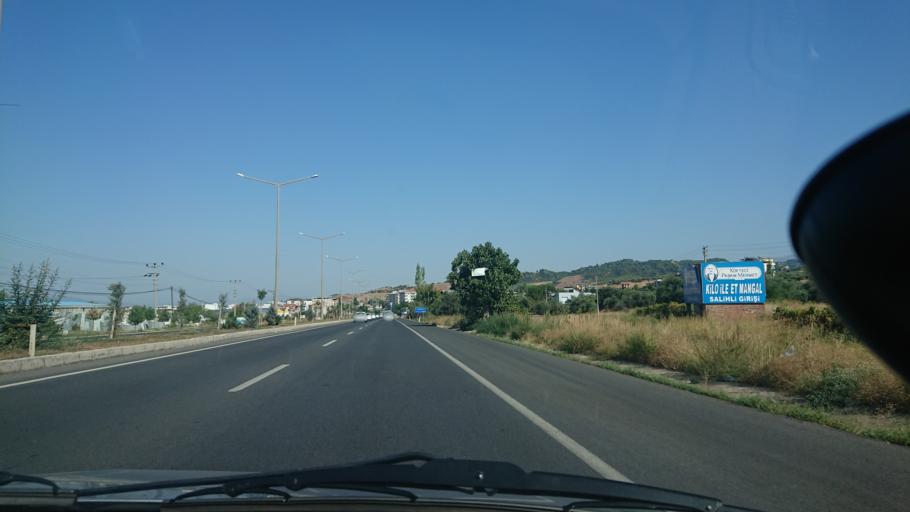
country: TR
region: Manisa
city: Ahmetli
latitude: 38.5124
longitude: 27.9242
